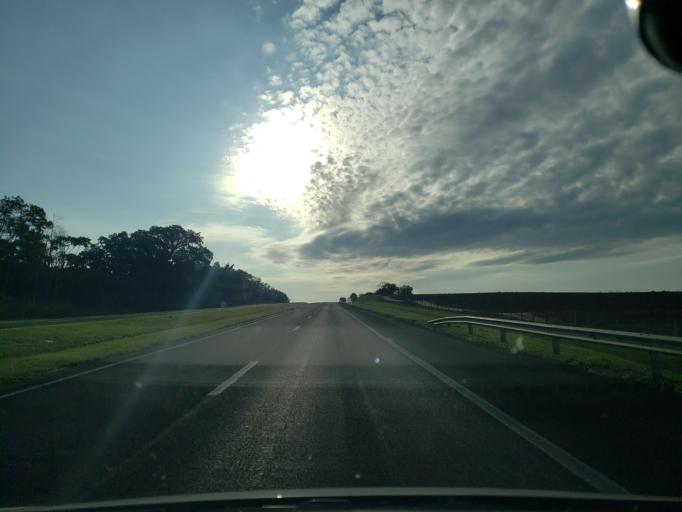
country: BR
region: Sao Paulo
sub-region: Valparaiso
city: Valparaiso
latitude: -21.1854
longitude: -50.9151
